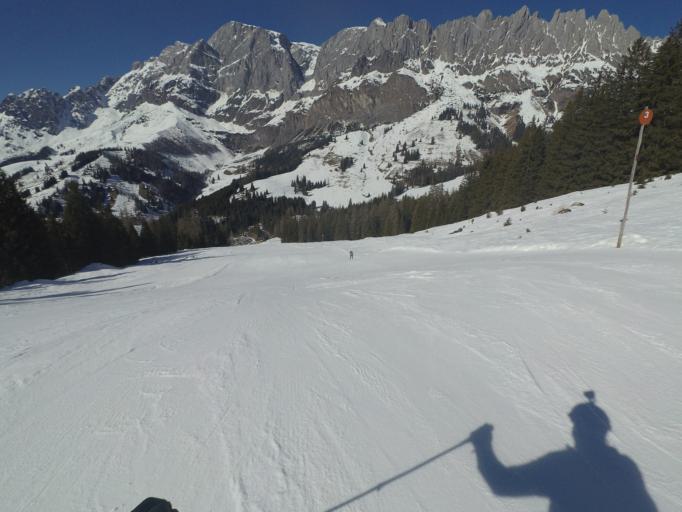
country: AT
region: Salzburg
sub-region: Politischer Bezirk Sankt Johann im Pongau
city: Muhlbach am Hochkonig
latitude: 47.3967
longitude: 13.1222
